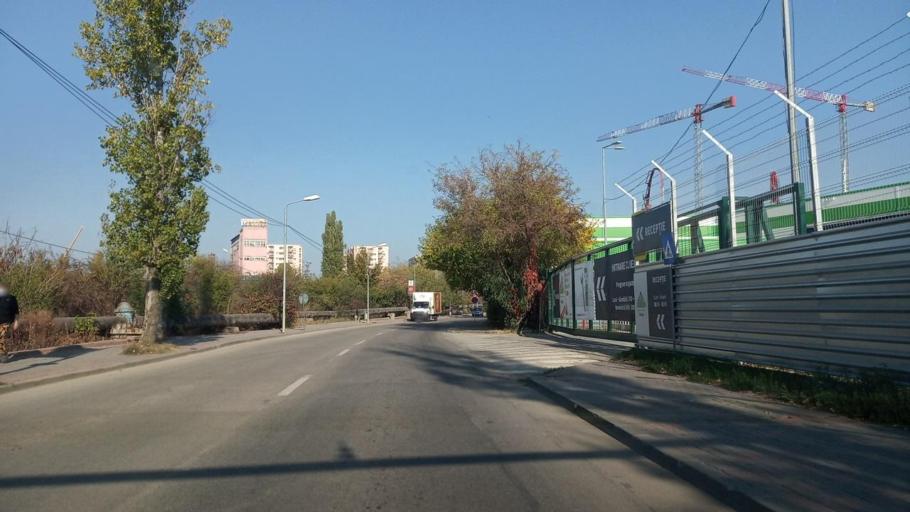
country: RO
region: Ilfov
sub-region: Comuna Glina
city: Catelu
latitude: 44.4092
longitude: 26.1943
